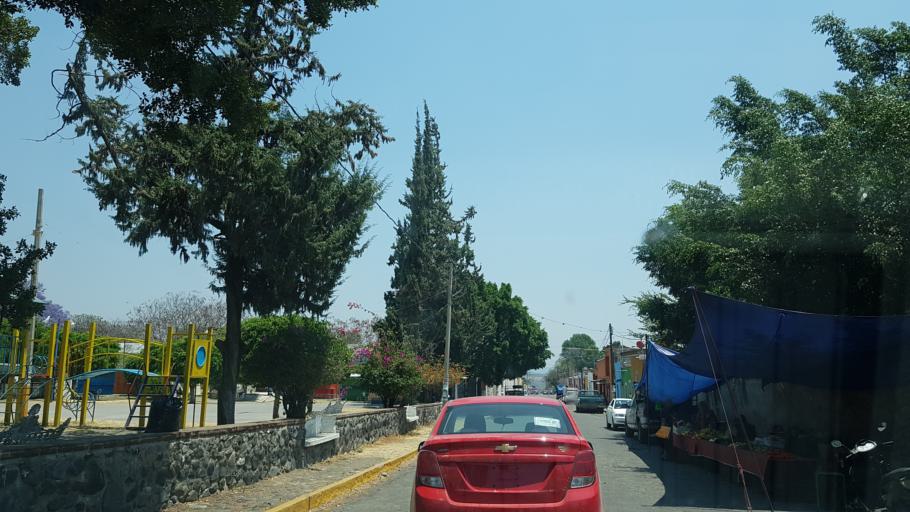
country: MX
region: Puebla
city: Huaquechula
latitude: 18.7688
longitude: -98.5416
